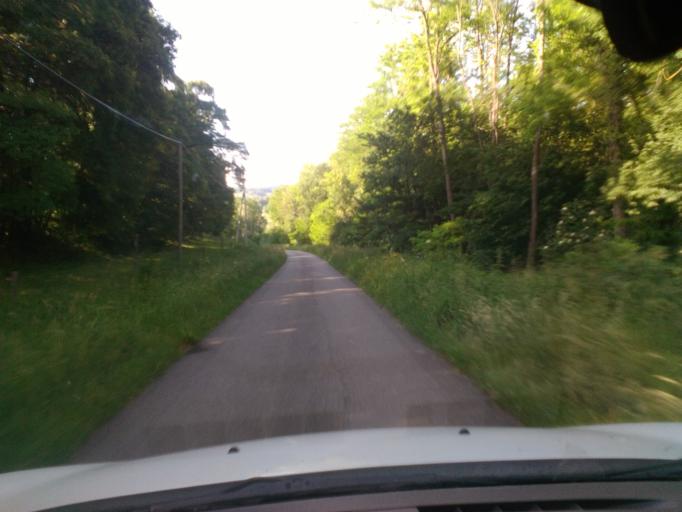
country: FR
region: Lorraine
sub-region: Departement des Vosges
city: Mirecourt
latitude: 48.2574
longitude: 6.2270
